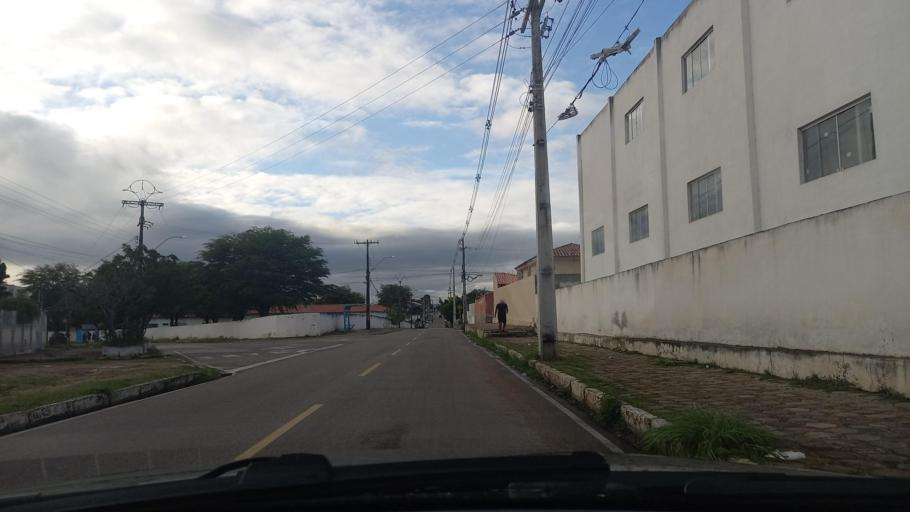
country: BR
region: Bahia
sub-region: Paulo Afonso
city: Paulo Afonso
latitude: -9.3954
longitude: -38.2317
